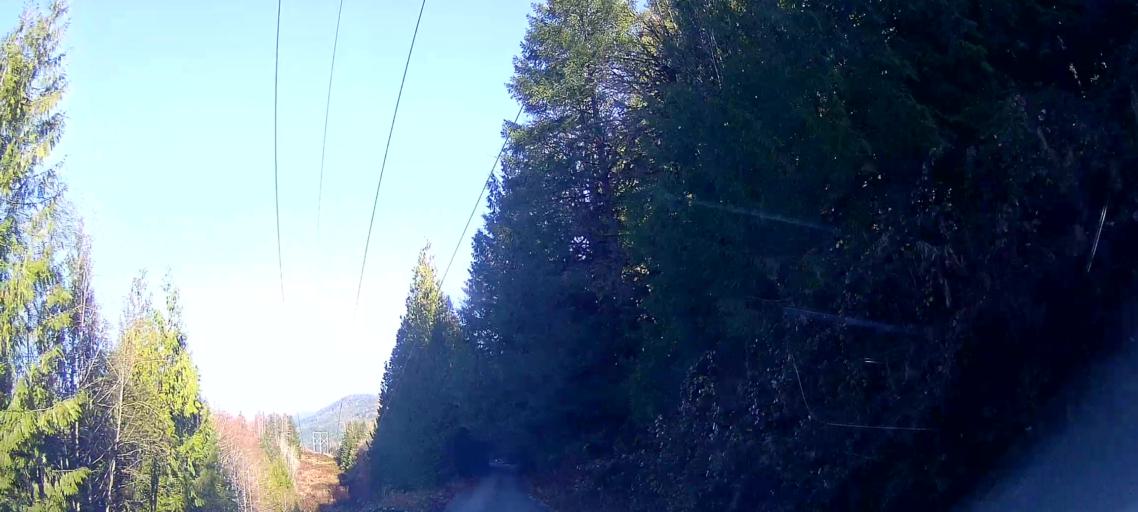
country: US
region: Washington
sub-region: Snohomish County
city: Darrington
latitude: 48.5590
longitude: -121.7242
